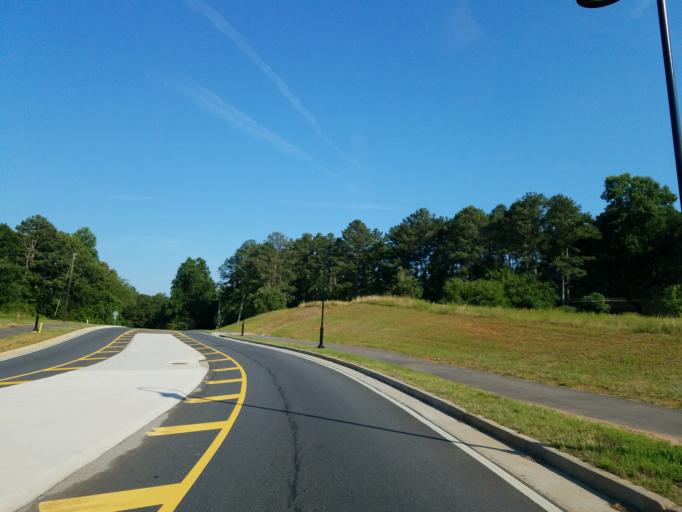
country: US
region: Georgia
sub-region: Fulton County
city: Milton
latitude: 34.1190
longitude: -84.3424
